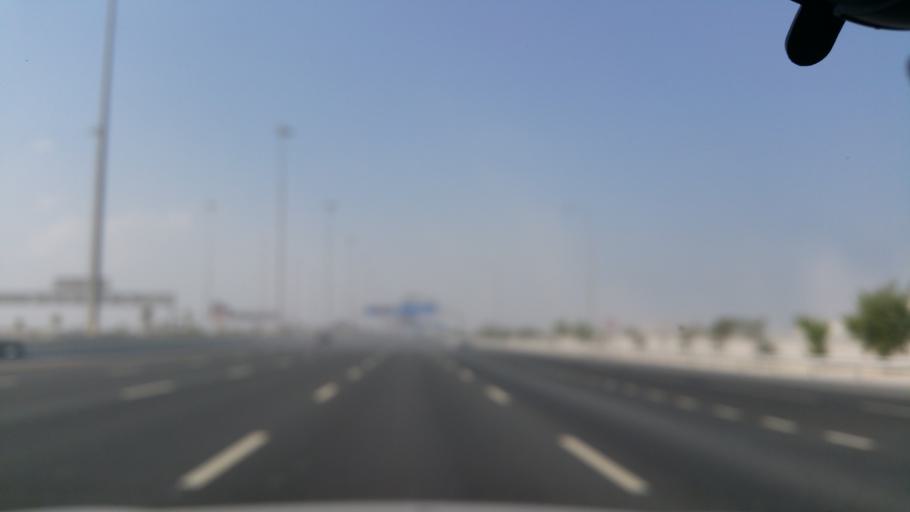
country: QA
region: Baladiyat Umm Salal
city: Umm Salal Muhammad
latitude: 25.4376
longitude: 51.4828
